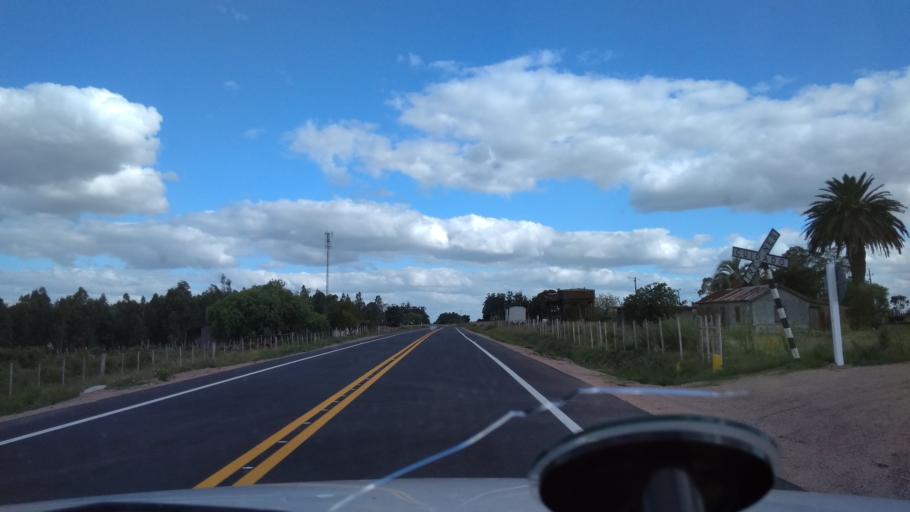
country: UY
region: Florida
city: Casupa
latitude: -33.9966
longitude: -55.6513
